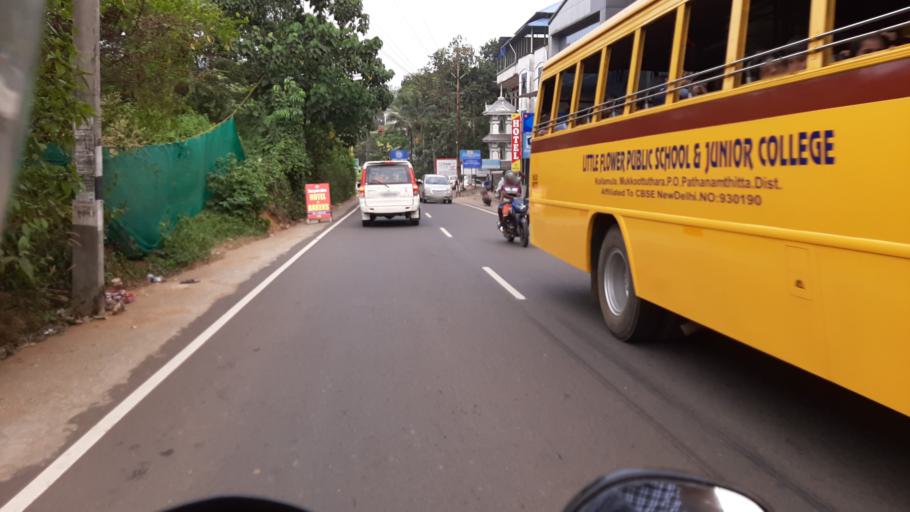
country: IN
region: Kerala
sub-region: Pattanamtitta
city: Pathanamthitta
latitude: 9.4472
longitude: 76.8753
